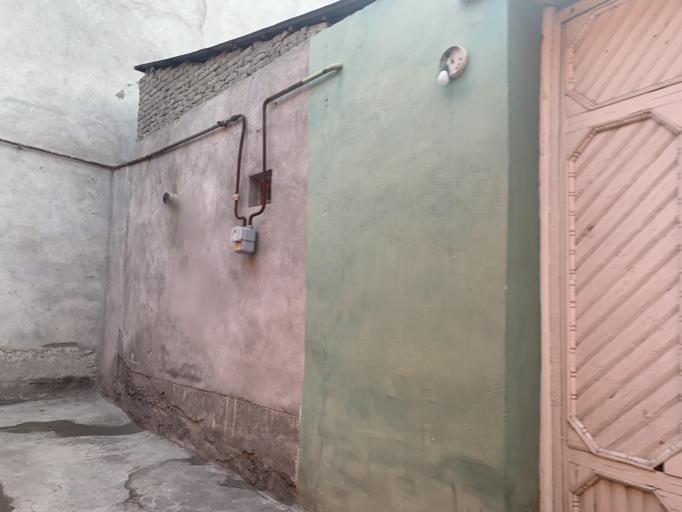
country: UZ
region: Fergana
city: Qo`qon
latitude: 40.5352
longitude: 70.9316
